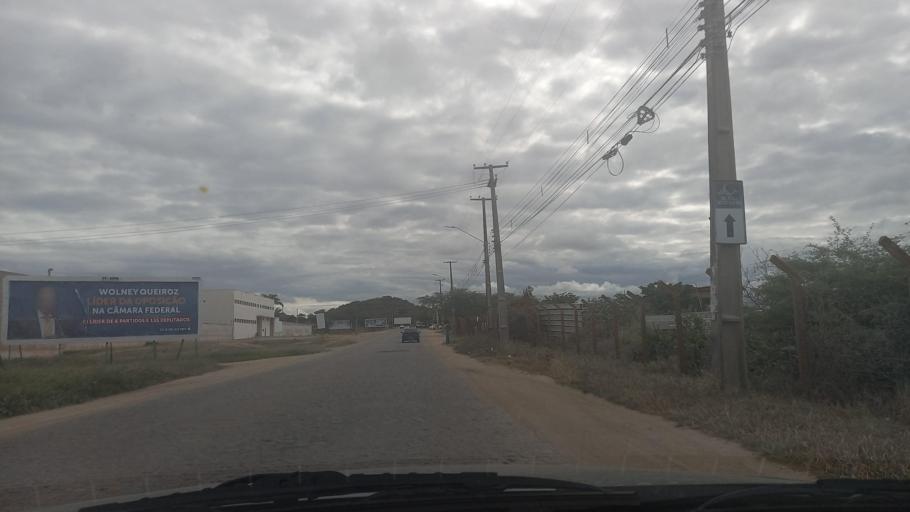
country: BR
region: Pernambuco
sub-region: Caruaru
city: Caruaru
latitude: -8.2895
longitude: -36.0162
